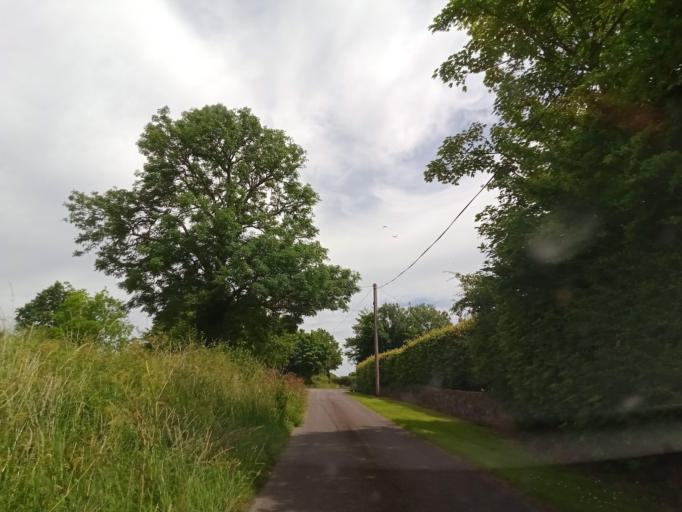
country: IE
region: Leinster
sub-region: Kilkenny
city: Thomastown
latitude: 52.5862
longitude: -7.1193
